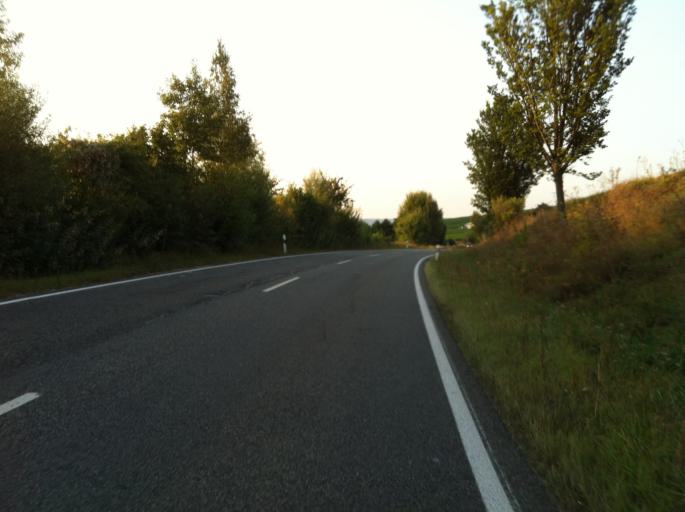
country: DE
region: Rheinland-Pfalz
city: Ingelheim am Rhein
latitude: 49.9514
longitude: 8.0725
